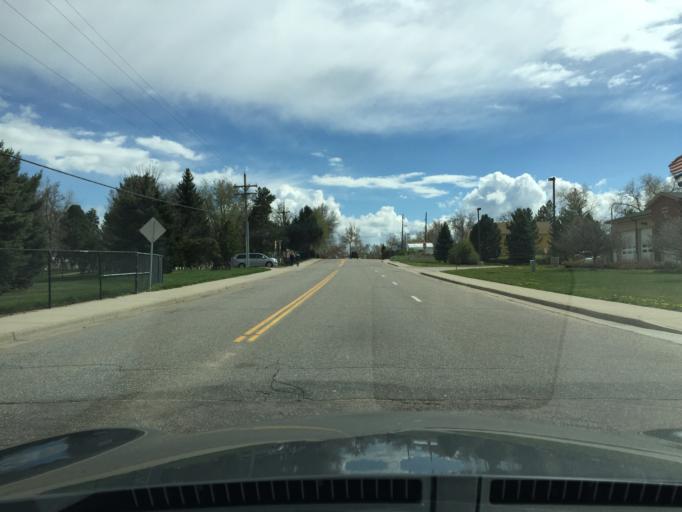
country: US
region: Colorado
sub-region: Boulder County
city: Lafayette
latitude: 40.0021
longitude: -105.0934
